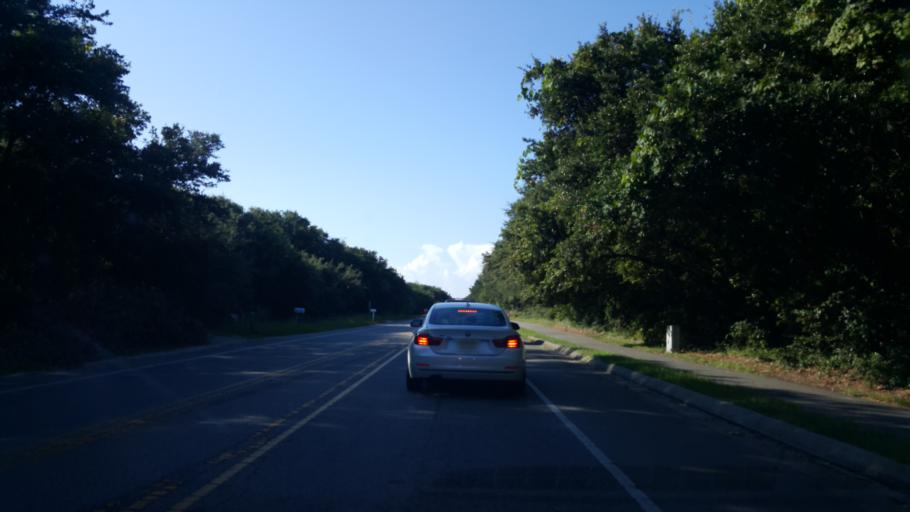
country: US
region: North Carolina
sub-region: Dare County
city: Southern Shores
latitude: 36.1355
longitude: -75.7354
